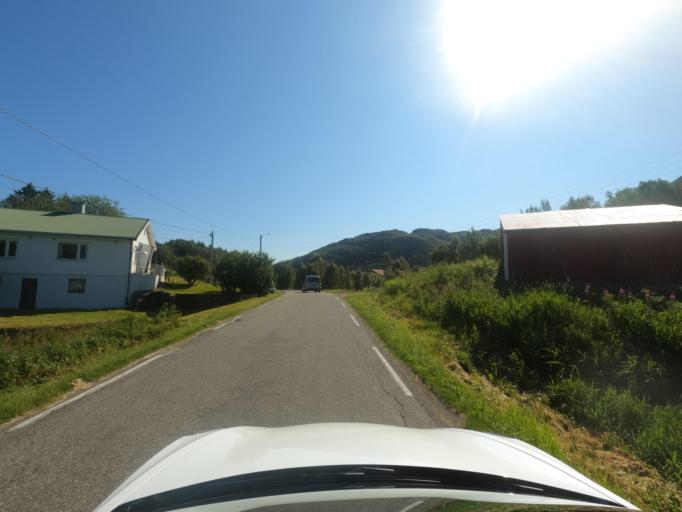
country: NO
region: Nordland
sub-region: Hadsel
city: Stokmarknes
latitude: 68.3022
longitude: 15.0200
